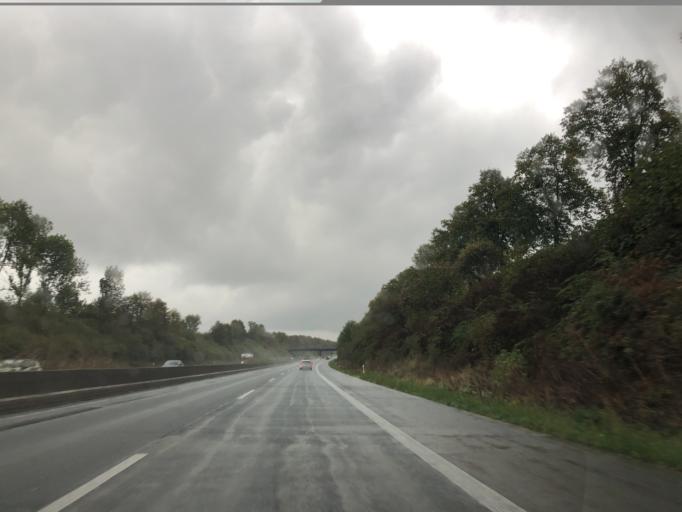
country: DE
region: North Rhine-Westphalia
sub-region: Regierungsbezirk Koln
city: Bergheim
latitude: 50.9328
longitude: 6.6611
